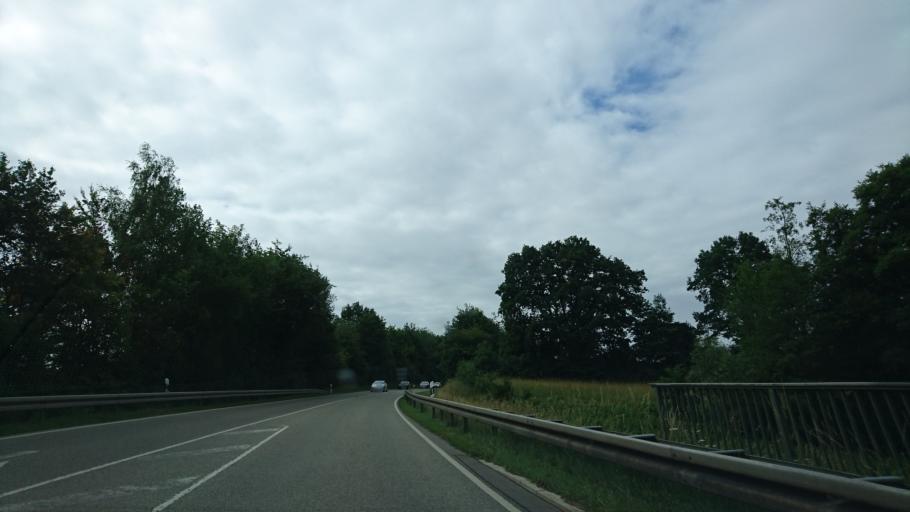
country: DE
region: Bavaria
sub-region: Regierungsbezirk Mittelfranken
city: Allersberg
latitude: 49.2400
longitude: 11.2148
